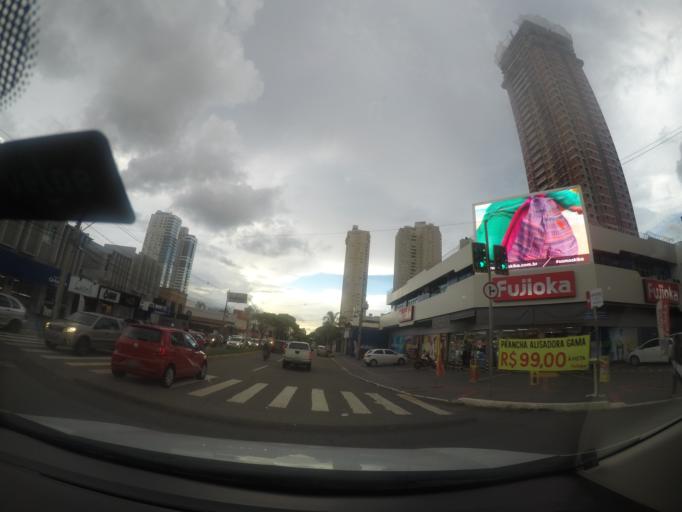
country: BR
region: Goias
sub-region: Goiania
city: Goiania
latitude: -16.7051
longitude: -49.2677
